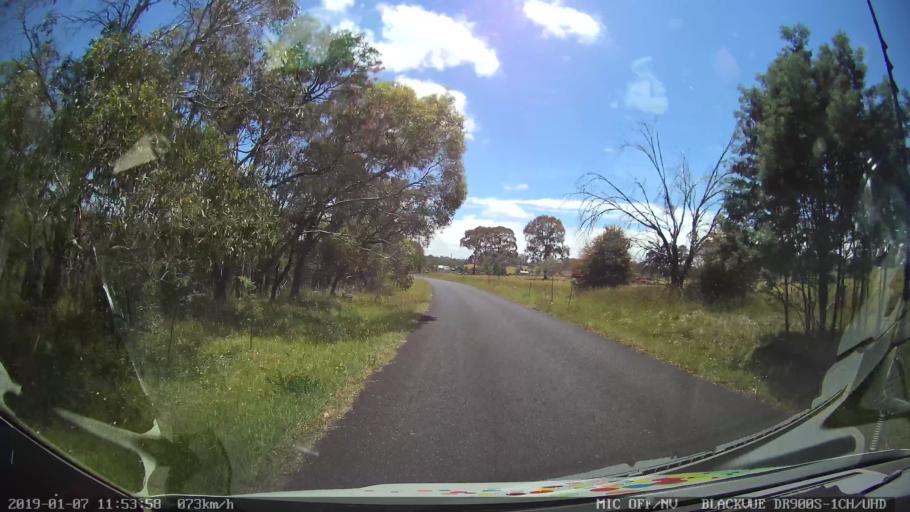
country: AU
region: New South Wales
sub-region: Guyra
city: Guyra
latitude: -30.3010
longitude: 151.6629
